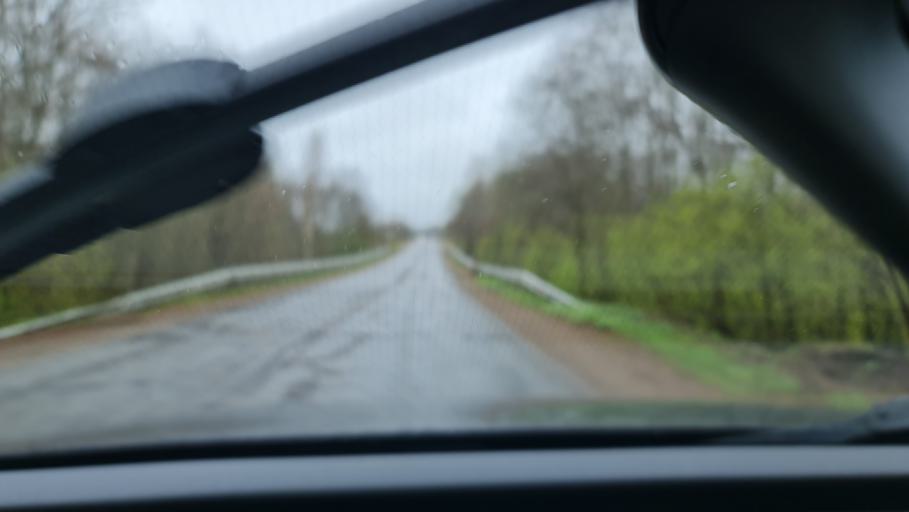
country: RU
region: Novgorod
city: Kresttsy
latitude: 58.0109
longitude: 32.7779
